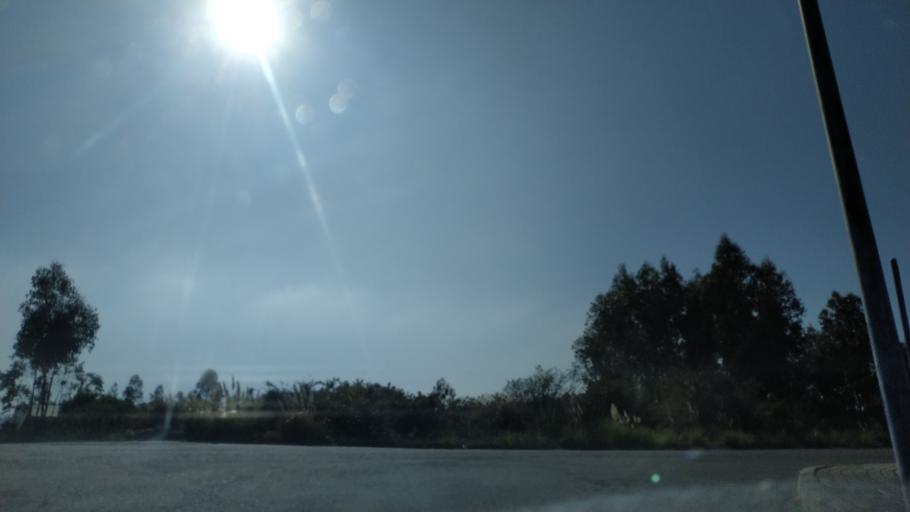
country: ES
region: Galicia
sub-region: Provincia da Coruna
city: Culleredo
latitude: 43.3224
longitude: -8.3890
